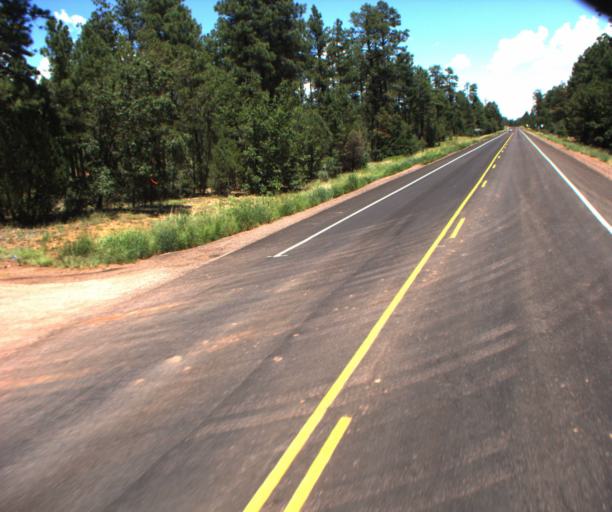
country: US
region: Arizona
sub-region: Navajo County
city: Show Low
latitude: 34.2045
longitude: -110.0809
